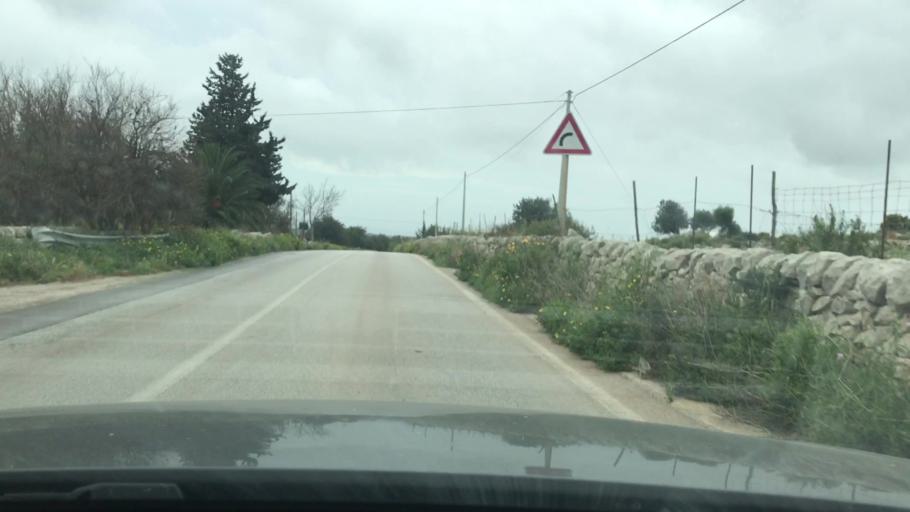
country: IT
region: Sicily
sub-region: Ragusa
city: Scicli
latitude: 36.8075
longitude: 14.7250
